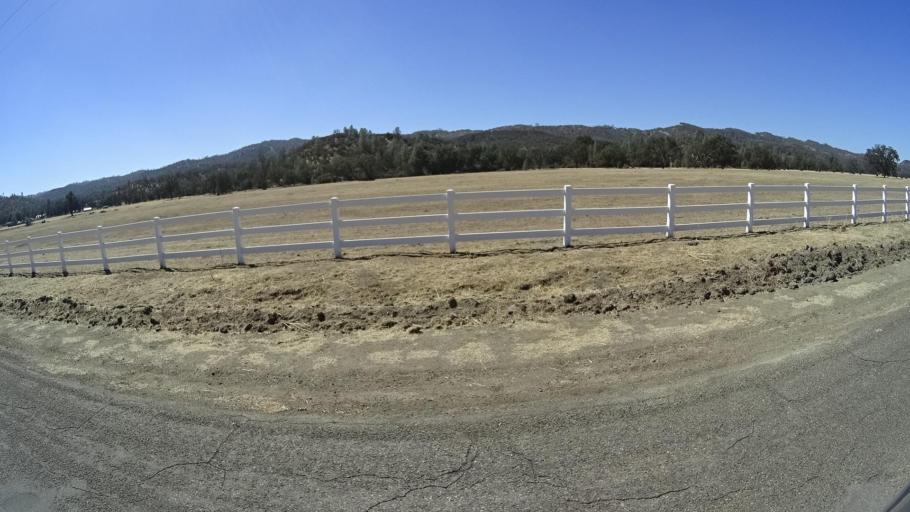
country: US
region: California
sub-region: Fresno County
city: Coalinga
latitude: 35.9327
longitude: -120.5094
